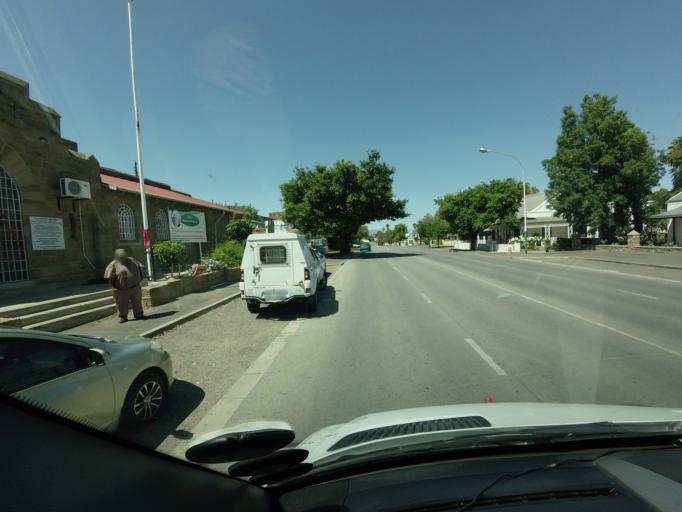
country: ZA
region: Western Cape
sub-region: Eden District Municipality
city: Oudtshoorn
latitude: -33.5829
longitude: 22.2046
